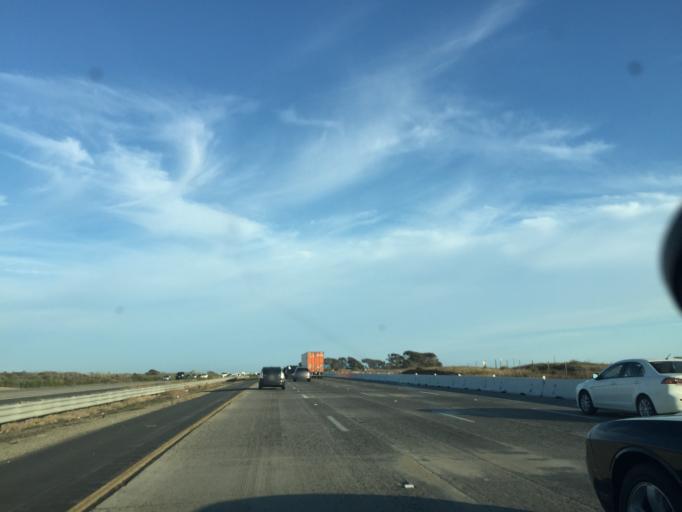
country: US
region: California
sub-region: San Diego County
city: Camp Pendleton South
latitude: 33.2784
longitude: -117.4471
